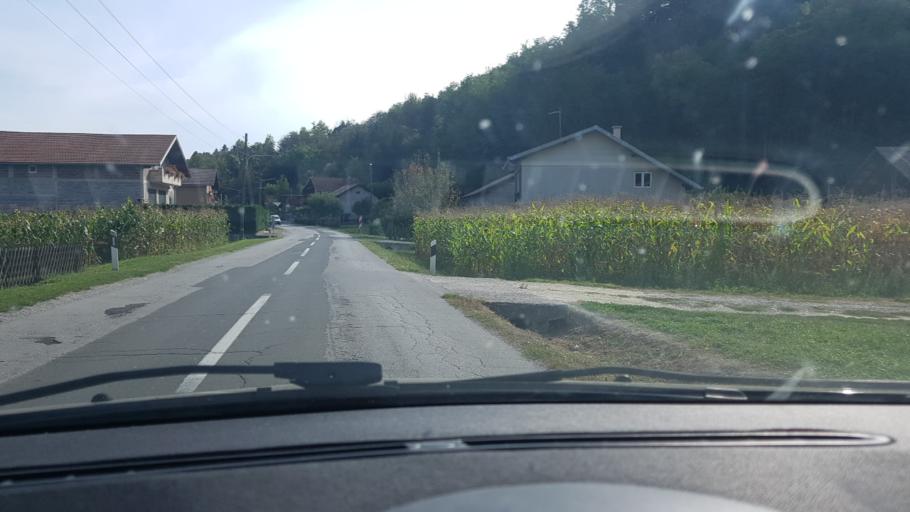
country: HR
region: Krapinsko-Zagorska
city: Zlatar
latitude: 46.1001
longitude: 16.0786
